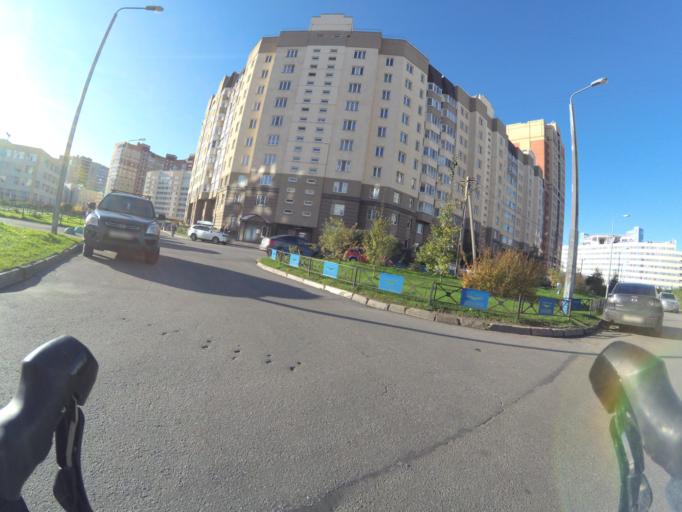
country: RU
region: Leningrad
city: Untolovo
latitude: 60.0004
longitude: 30.2035
